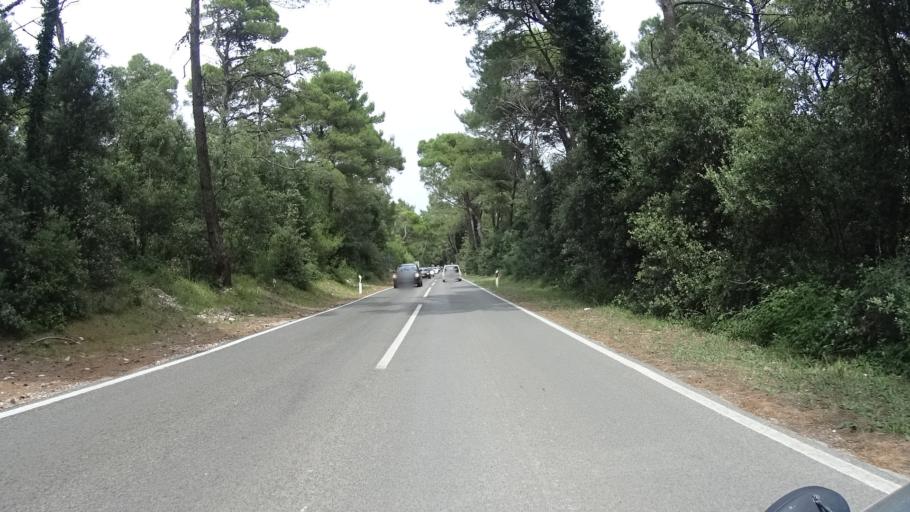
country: HR
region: Istarska
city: Medulin
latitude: 44.8105
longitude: 13.9089
